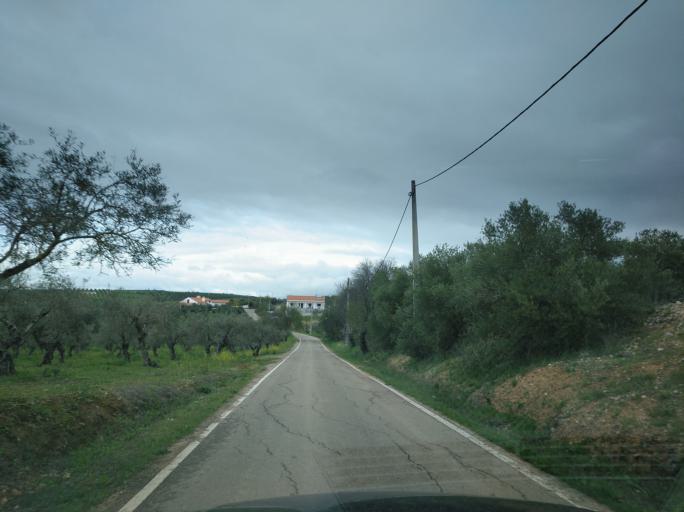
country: PT
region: Portalegre
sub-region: Campo Maior
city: Campo Maior
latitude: 38.9896
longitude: -7.0460
